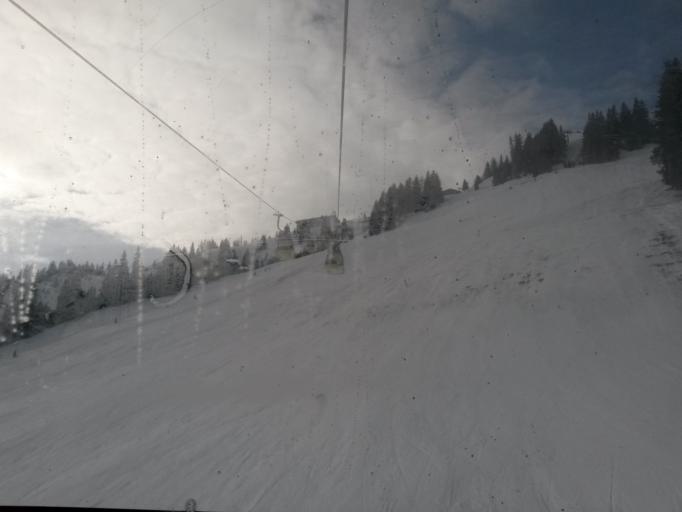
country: AT
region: Salzburg
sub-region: Politischer Bezirk Sankt Johann im Pongau
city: Dorfgastein
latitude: 47.2344
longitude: 13.1758
